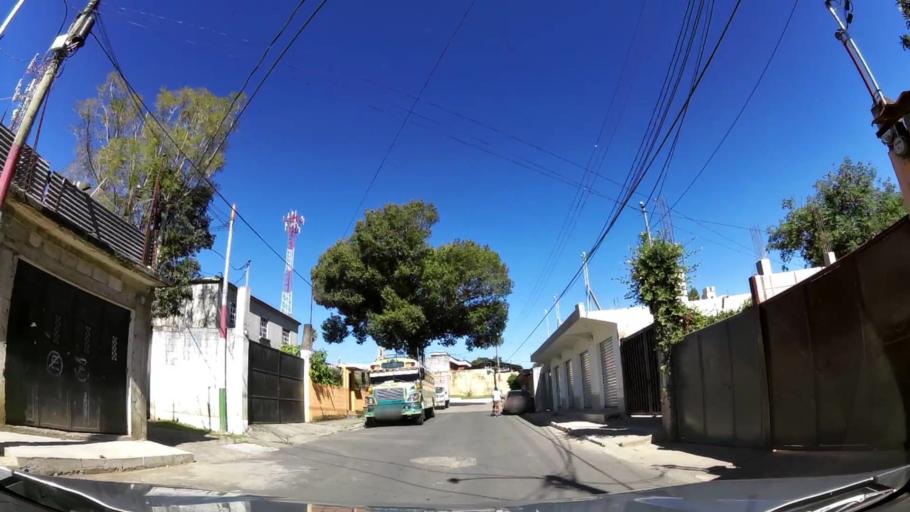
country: GT
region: Guatemala
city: Fraijanes
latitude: 14.4648
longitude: -90.4396
